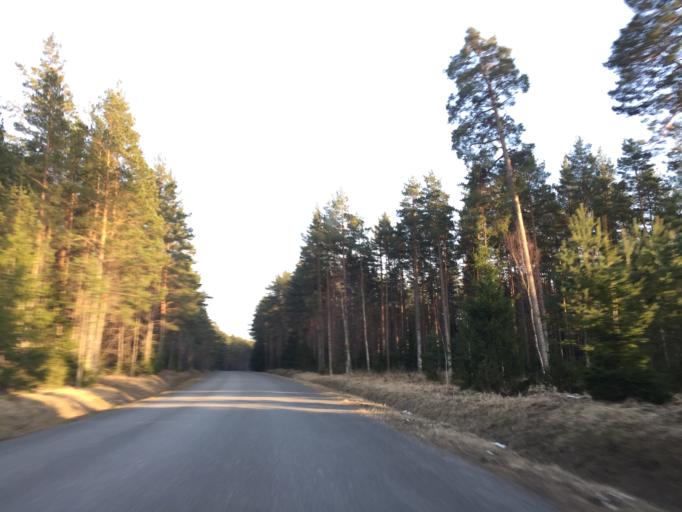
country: EE
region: Laeaene
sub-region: Lihula vald
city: Lihula
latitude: 58.4701
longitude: 23.7144
